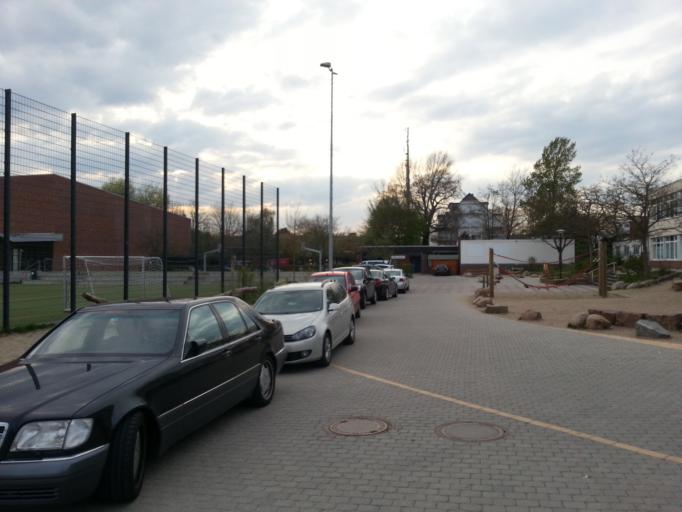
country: DE
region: Schleswig-Holstein
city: Timmendorfer Strand
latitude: 53.9947
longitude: 10.7848
